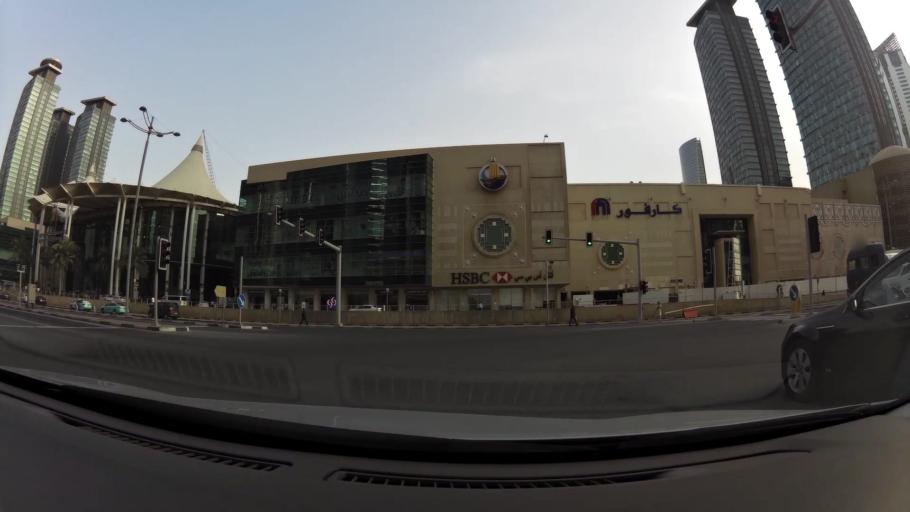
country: QA
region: Baladiyat ad Dawhah
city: Doha
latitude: 25.3262
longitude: 51.5296
